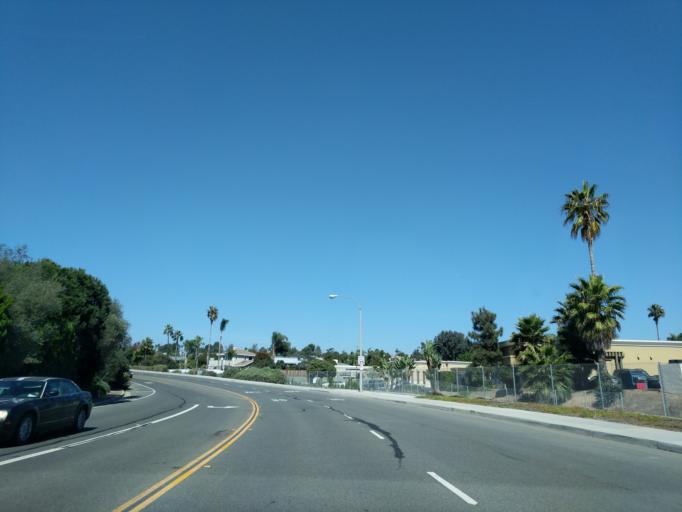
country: US
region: California
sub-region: Orange County
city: San Clemente
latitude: 33.4433
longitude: -117.6440
